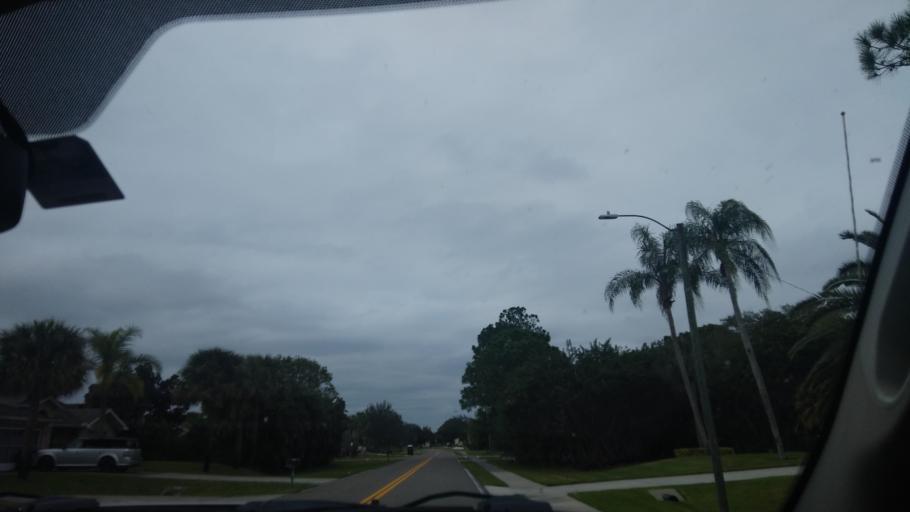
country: US
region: Florida
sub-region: Indian River County
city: Sebastian
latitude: 27.7612
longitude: -80.4872
